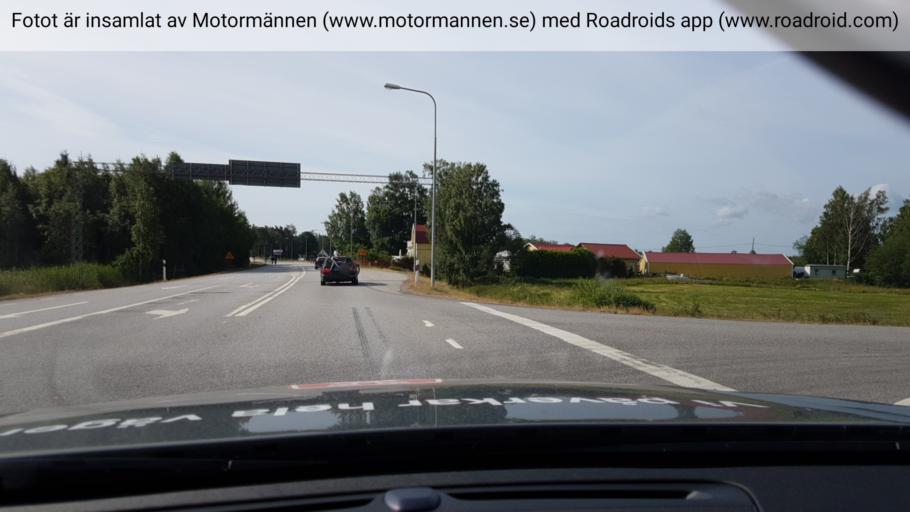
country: SE
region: Vaestra Goetaland
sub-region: Karlsborgs Kommun
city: Karlsborg
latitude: 58.5709
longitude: 14.4951
